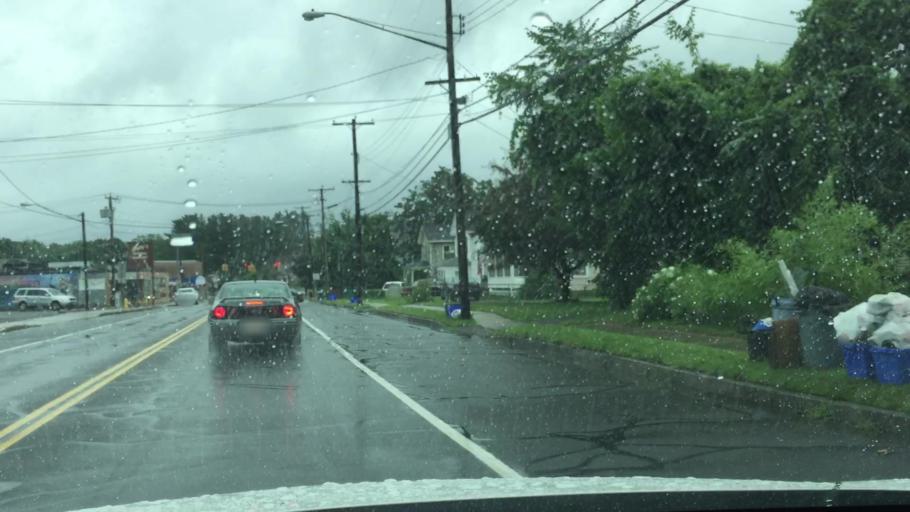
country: US
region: Massachusetts
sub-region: Berkshire County
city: Pittsfield
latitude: 42.4678
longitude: -73.2510
